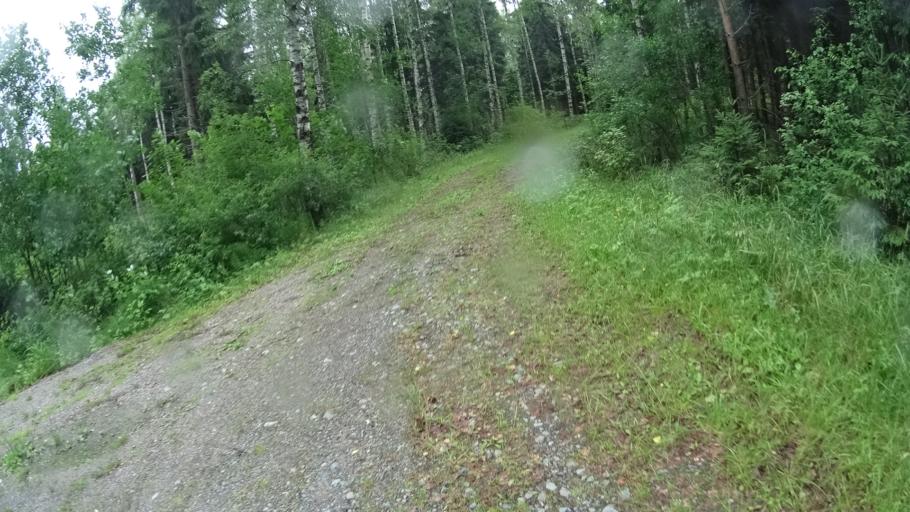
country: FI
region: Uusimaa
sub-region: Helsinki
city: Karkkila
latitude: 60.5777
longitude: 24.2643
